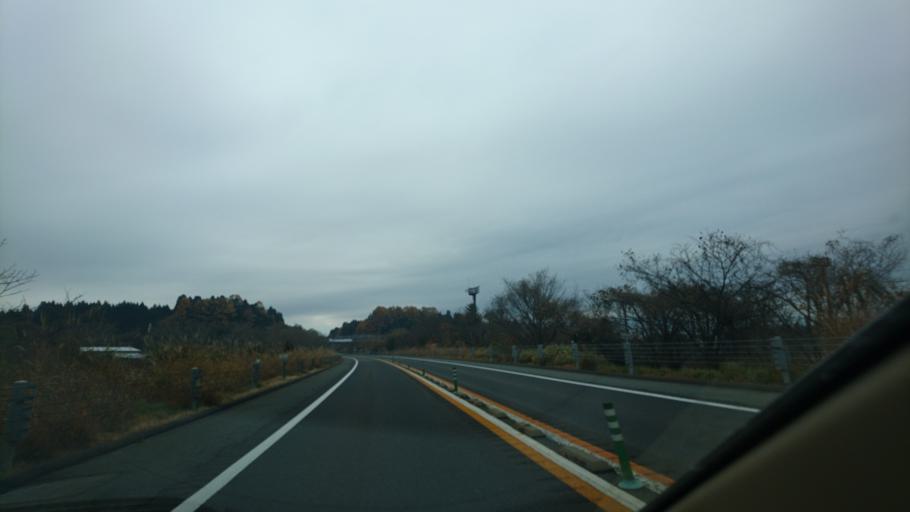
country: JP
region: Iwate
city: Kitakami
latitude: 39.2792
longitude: 141.0424
